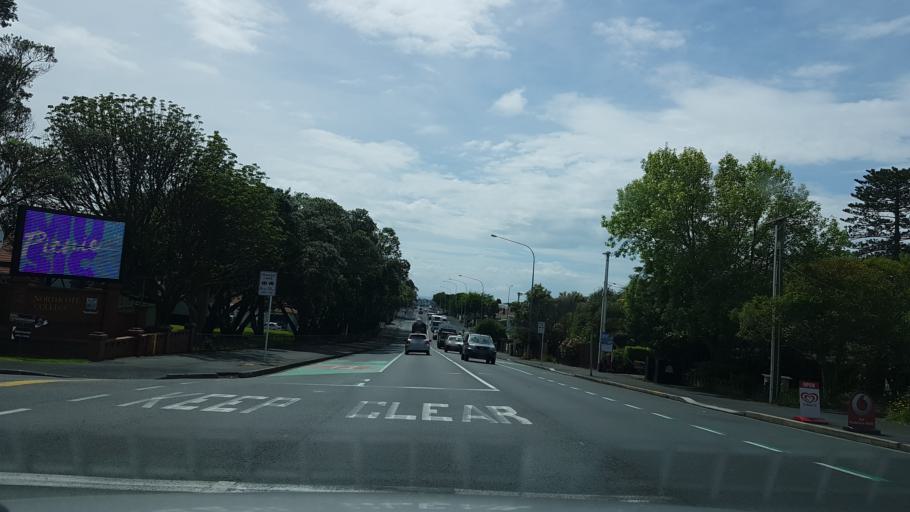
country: NZ
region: Auckland
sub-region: Auckland
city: North Shore
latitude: -36.8102
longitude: 174.7332
